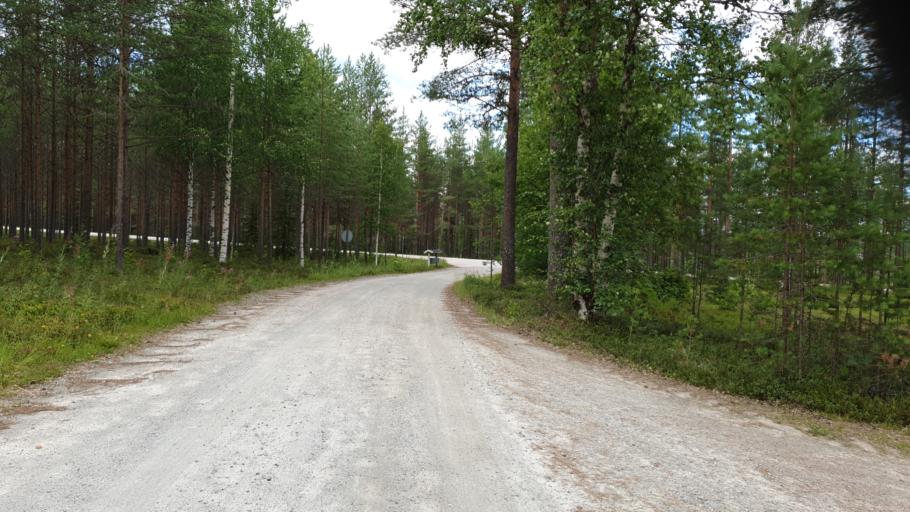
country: FI
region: Kainuu
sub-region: Kehys-Kainuu
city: Kuhmo
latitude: 64.3843
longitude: 29.8082
